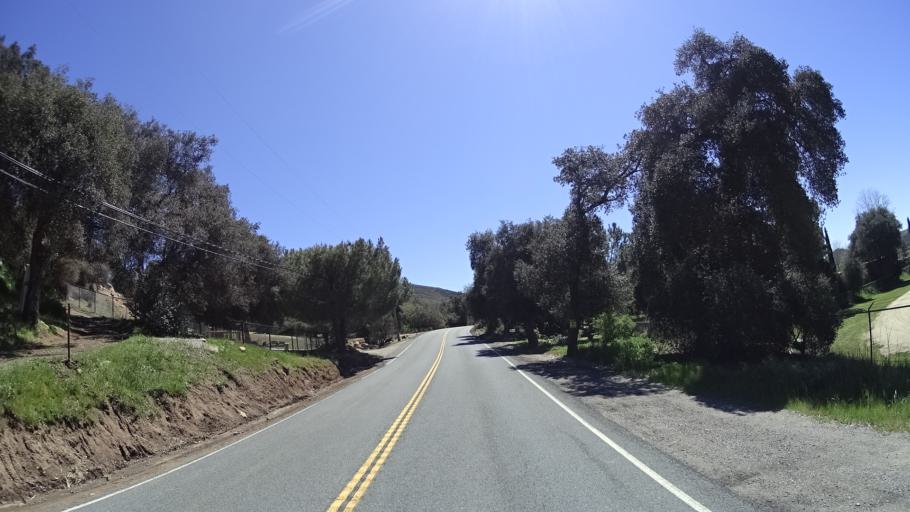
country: US
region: California
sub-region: San Diego County
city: Descanso
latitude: 32.8576
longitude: -116.5945
